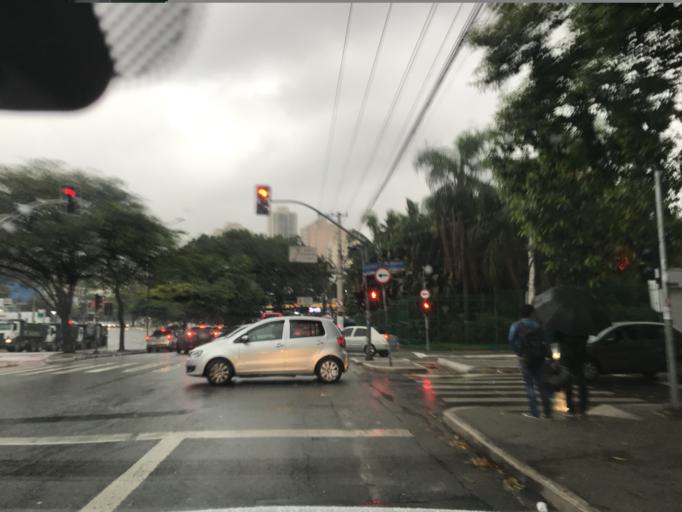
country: BR
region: Sao Paulo
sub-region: Sao Paulo
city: Sao Paulo
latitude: -23.5289
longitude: -46.6763
